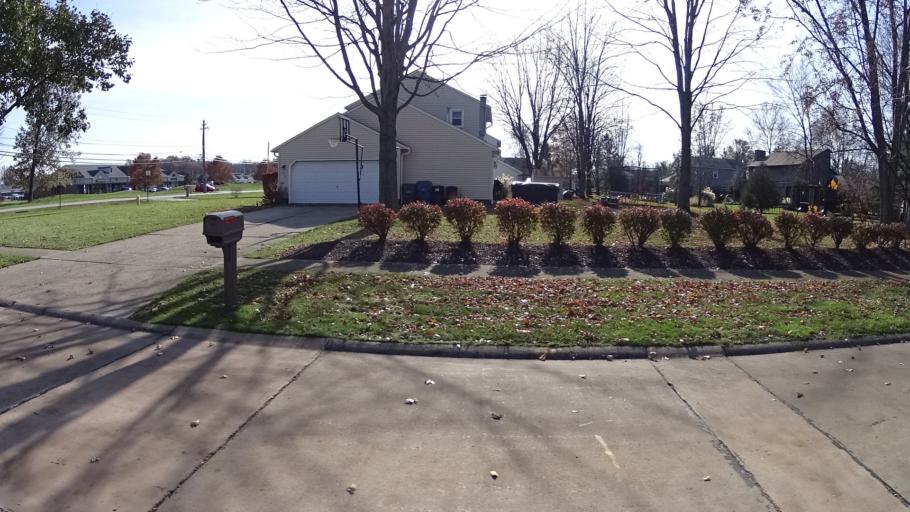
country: US
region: Ohio
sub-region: Lorain County
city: Avon Lake
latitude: 41.4964
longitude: -81.9888
